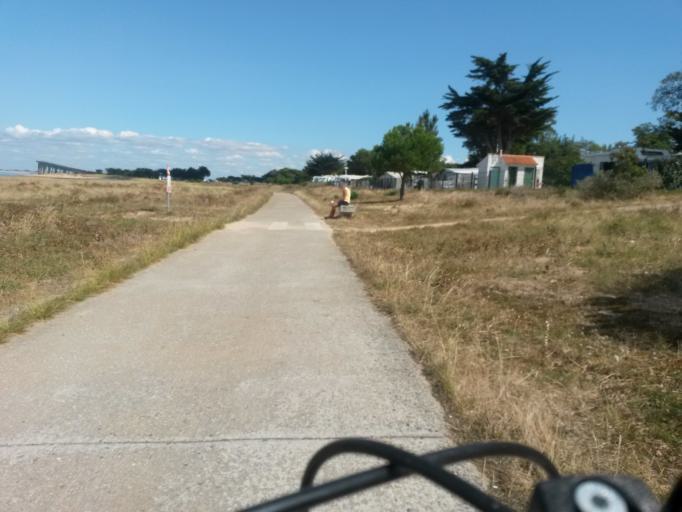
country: FR
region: Poitou-Charentes
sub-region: Departement de la Charente-Maritime
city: Rivedoux-Plage
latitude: 46.1598
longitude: -1.2681
